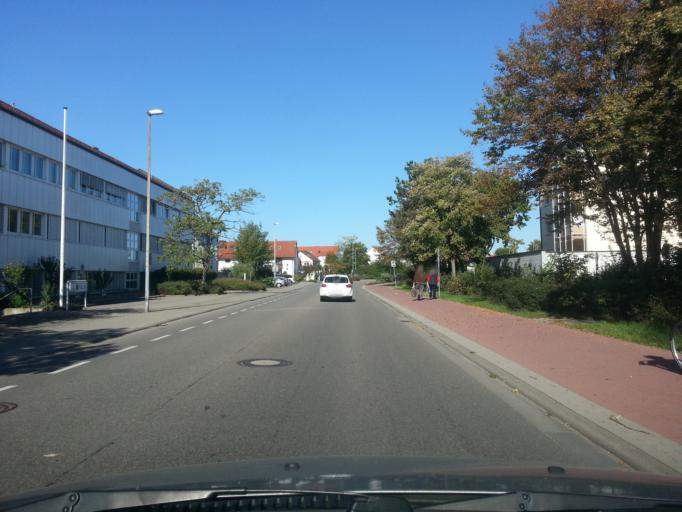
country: DE
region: Rheinland-Pfalz
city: Schifferstadt
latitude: 49.3832
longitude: 8.3914
